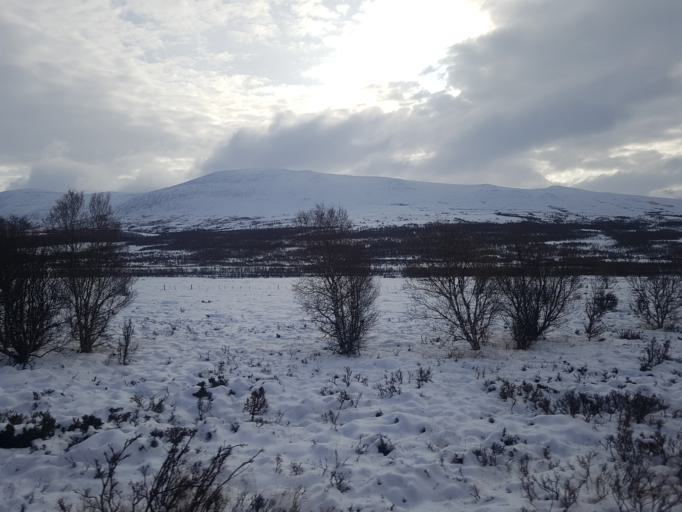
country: NO
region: Oppland
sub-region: Dovre
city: Dovre
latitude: 62.1331
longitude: 9.3154
